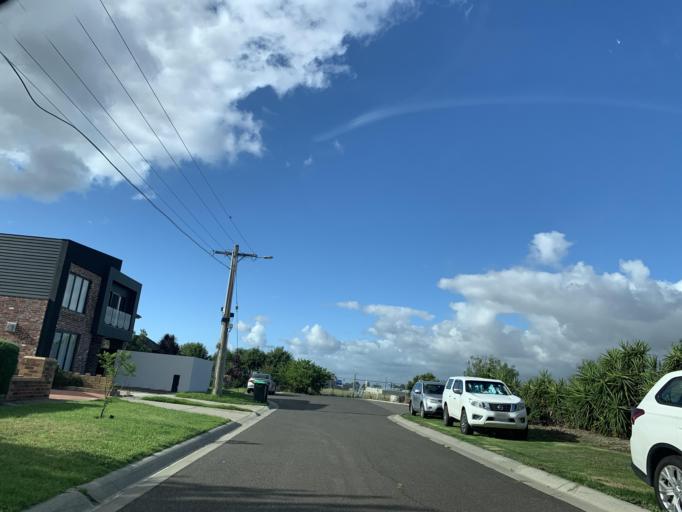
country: AU
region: Victoria
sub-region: Moreland
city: Oak Park
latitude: -37.7278
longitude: 144.9128
